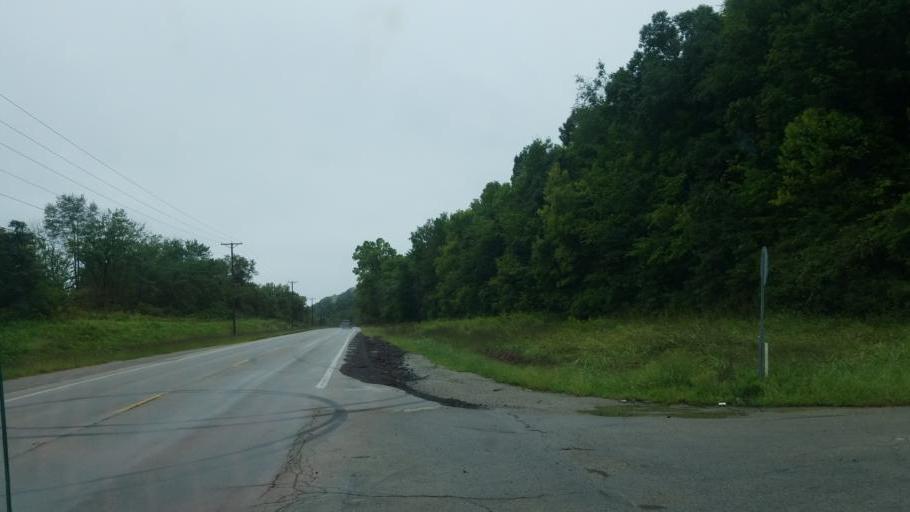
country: US
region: Kentucky
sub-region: Mason County
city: Maysville
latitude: 38.6449
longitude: -83.7053
